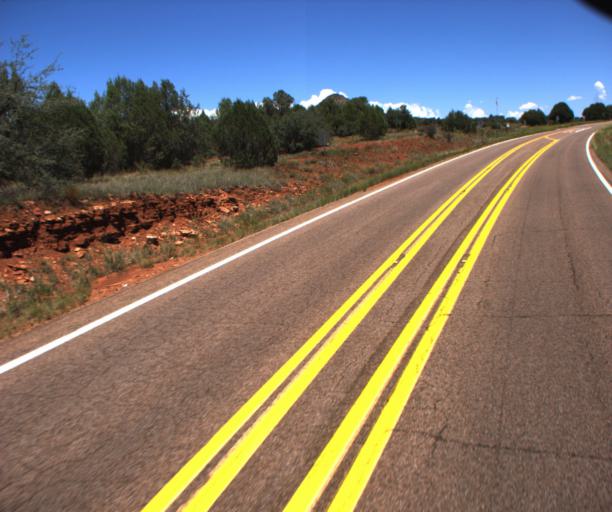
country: US
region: Arizona
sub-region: Navajo County
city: Cibecue
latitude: 33.9555
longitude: -110.3317
